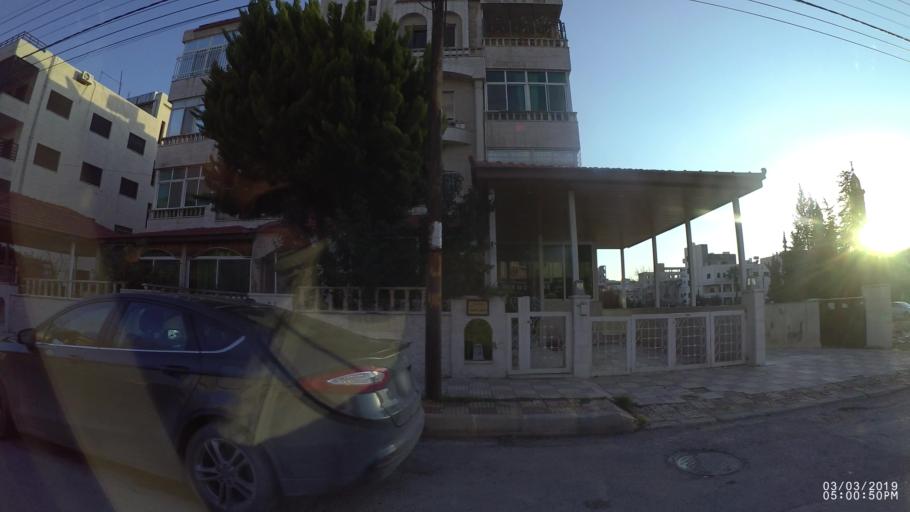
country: JO
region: Amman
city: Al Jubayhah
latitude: 31.9923
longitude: 35.8724
